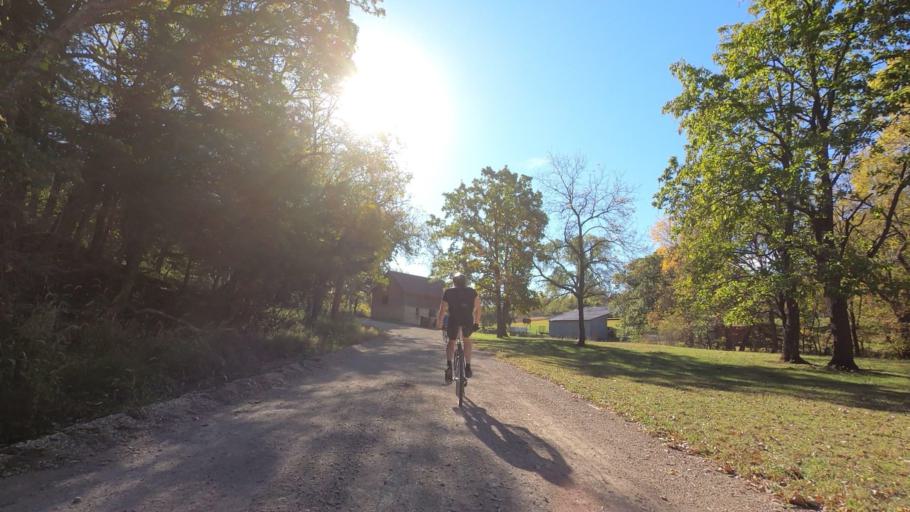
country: US
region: Kansas
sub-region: Pottawatomie County
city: Westmoreland
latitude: 39.4832
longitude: -96.5977
